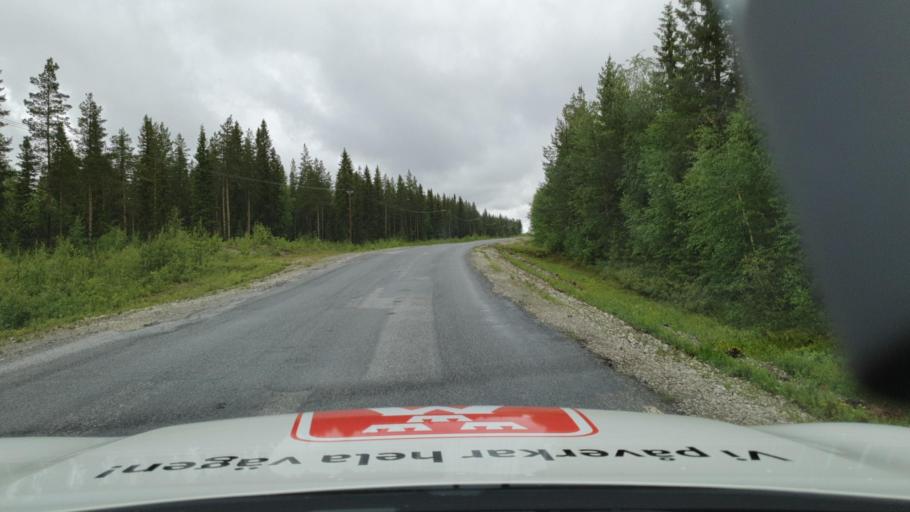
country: SE
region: Vaesterbotten
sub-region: Dorotea Kommun
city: Dorotea
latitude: 64.1576
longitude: 16.6489
